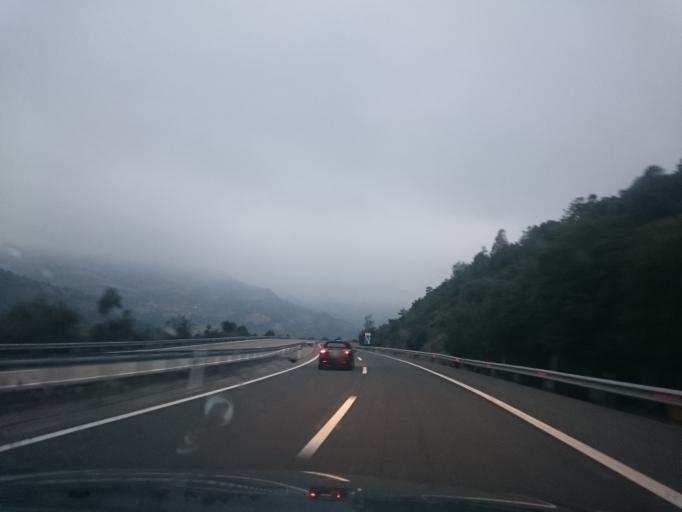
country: ES
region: Asturias
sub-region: Province of Asturias
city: Pola de Lena
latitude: 43.0459
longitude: -5.8196
